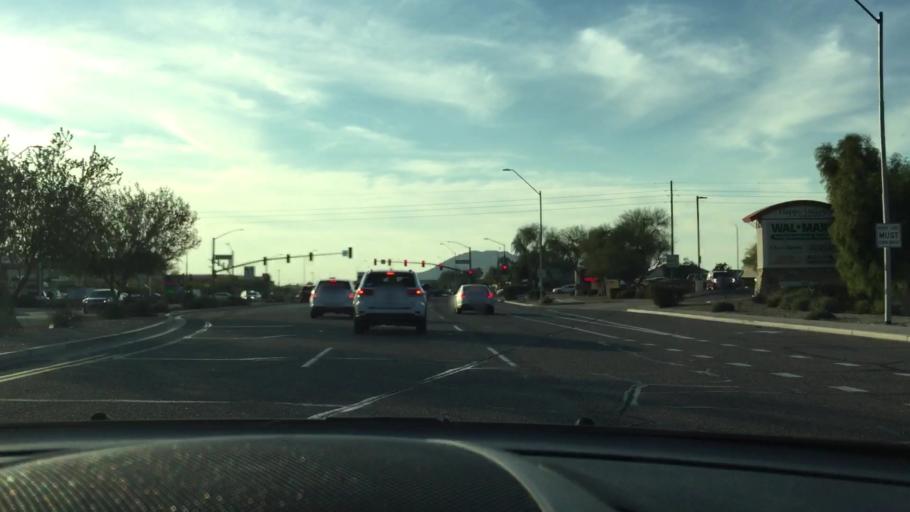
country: US
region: Arizona
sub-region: Maricopa County
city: Sun City
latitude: 33.7123
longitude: -112.2015
